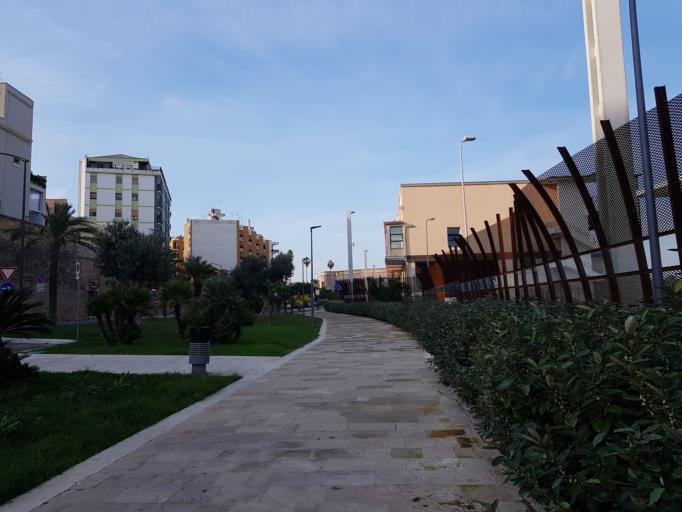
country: IT
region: Apulia
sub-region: Provincia di Brindisi
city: Brindisi
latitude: 40.6378
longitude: 17.9496
